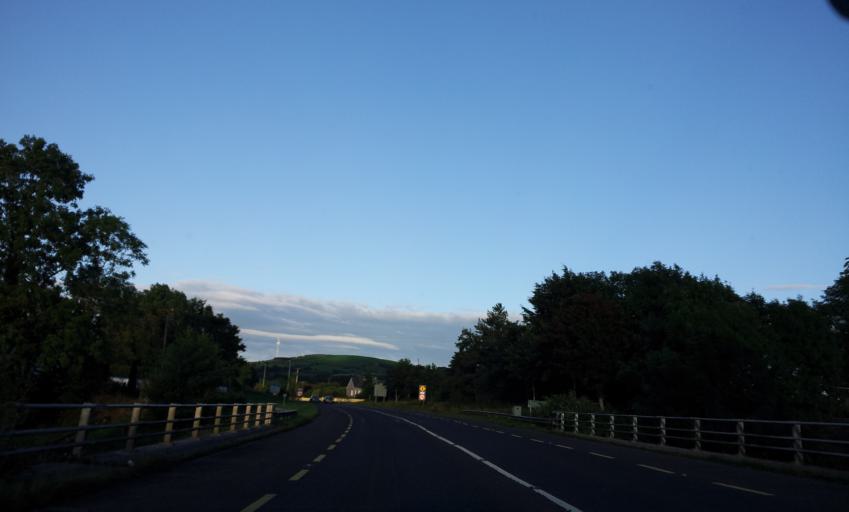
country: IE
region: Munster
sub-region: County Limerick
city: Abbeyfeale
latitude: 52.3823
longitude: -9.2222
